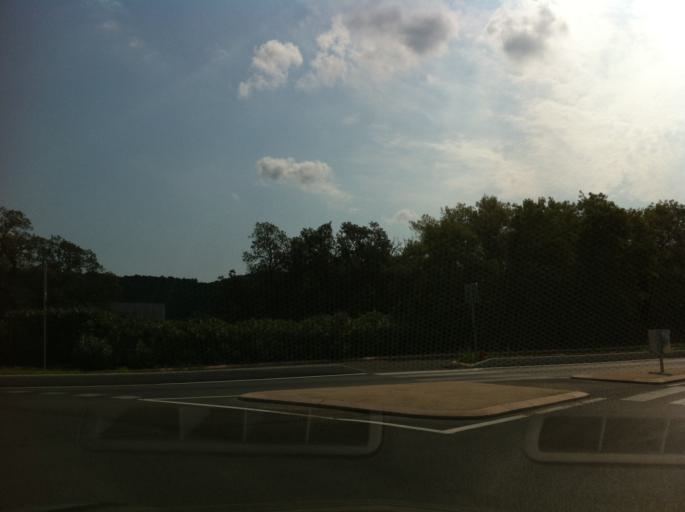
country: FR
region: Provence-Alpes-Cote d'Azur
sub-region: Departement du Var
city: Gassin
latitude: 43.2499
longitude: 6.5728
